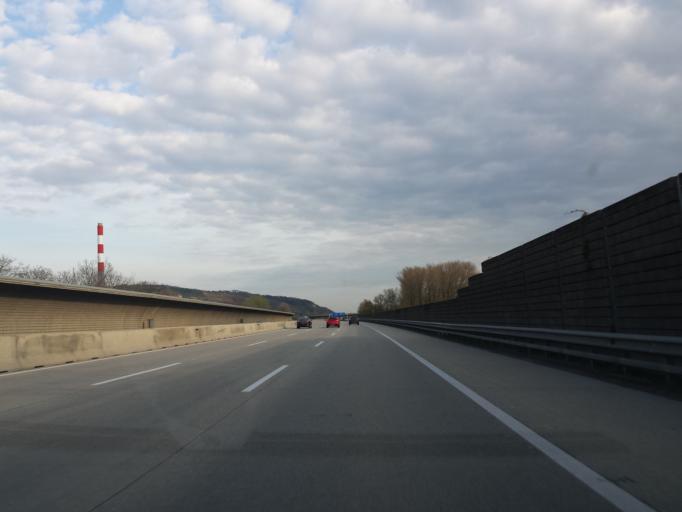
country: AT
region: Lower Austria
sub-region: Politischer Bezirk Korneuburg
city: Korneuburg
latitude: 48.3363
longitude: 16.3283
